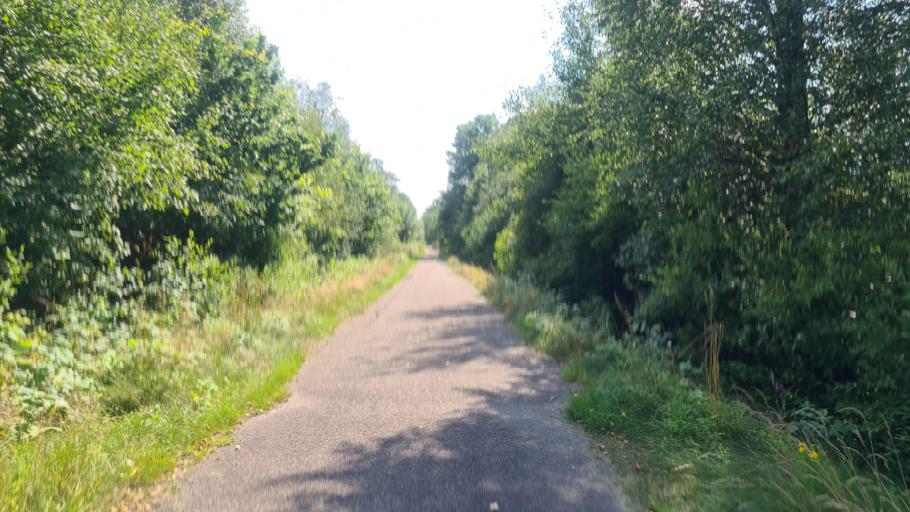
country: SE
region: Kronoberg
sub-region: Ljungby Kommun
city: Ljungby
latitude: 56.7969
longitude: 13.9102
